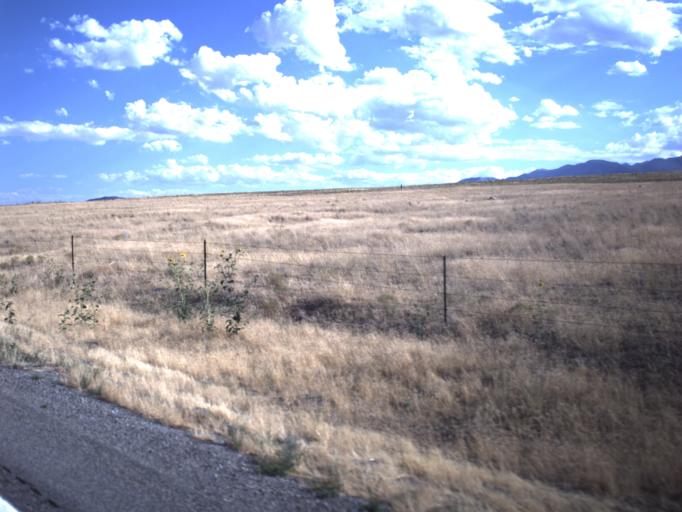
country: US
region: Utah
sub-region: Tooele County
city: Grantsville
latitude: 40.6357
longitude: -112.5189
